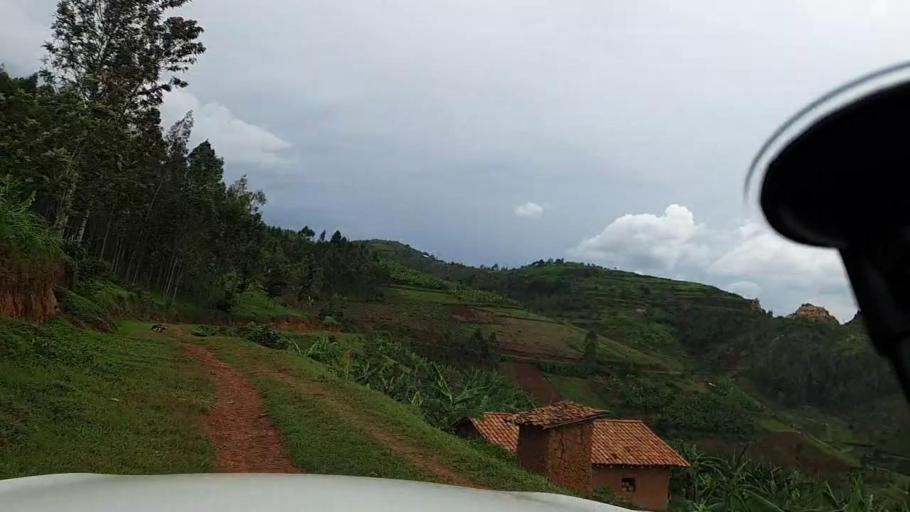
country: RW
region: Southern Province
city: Gitarama
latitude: -2.0781
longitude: 29.6425
